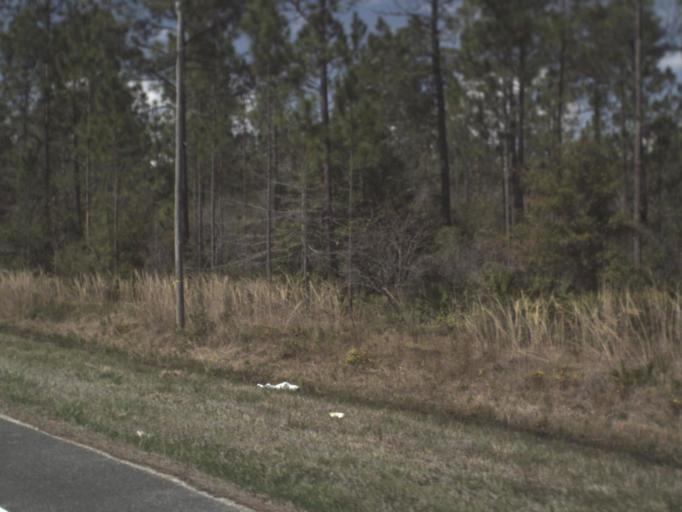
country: US
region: Florida
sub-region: Gadsden County
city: Midway
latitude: 30.3887
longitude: -84.5982
